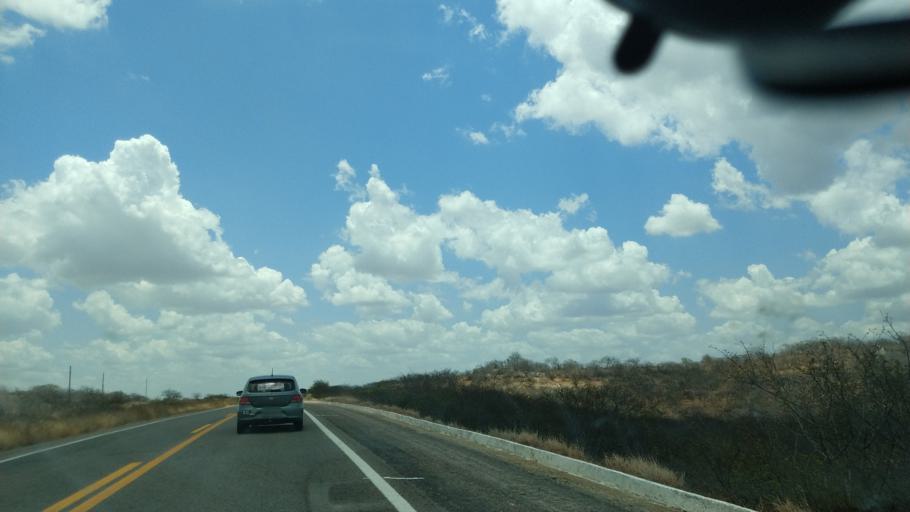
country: BR
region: Rio Grande do Norte
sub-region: Cerro Cora
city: Cerro Cora
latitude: -6.2029
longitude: -36.3302
